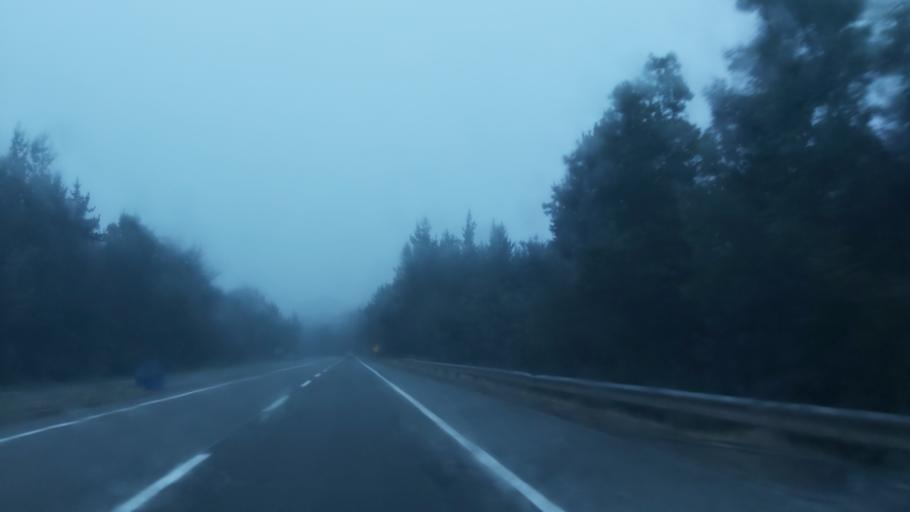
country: CL
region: Biobio
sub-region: Provincia de Concepcion
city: Penco
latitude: -36.7490
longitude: -72.9220
